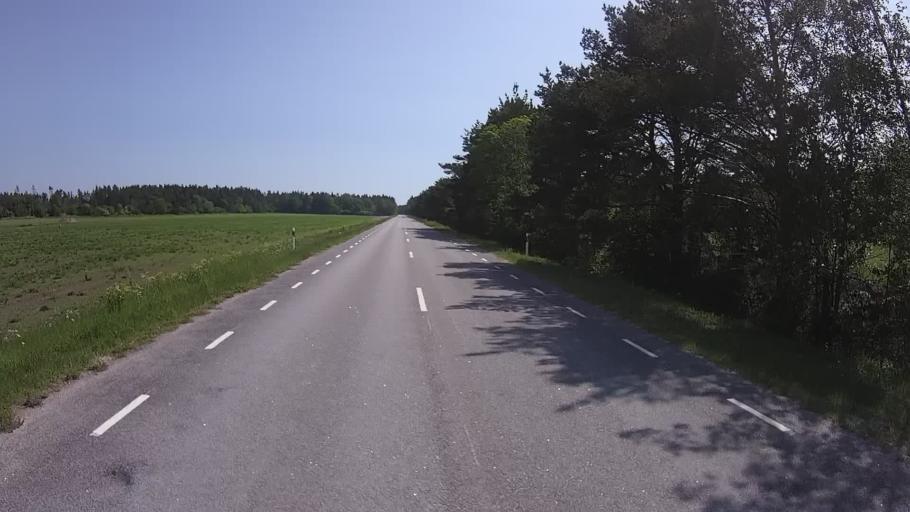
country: EE
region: Saare
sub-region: Kuressaare linn
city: Kuressaare
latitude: 58.3611
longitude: 22.0606
